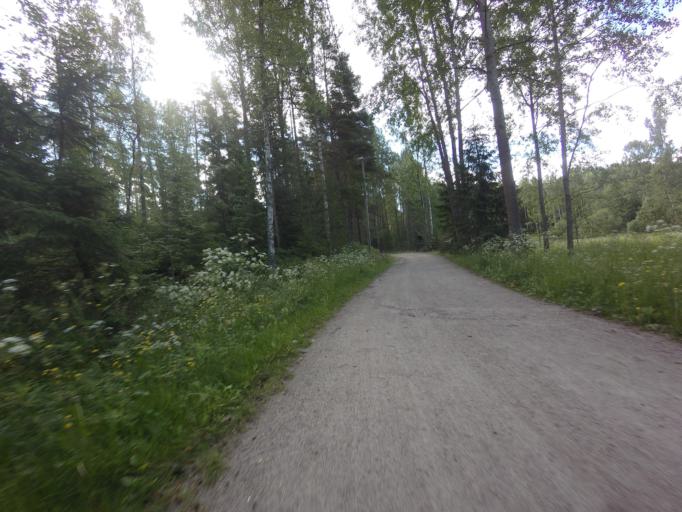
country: FI
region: Uusimaa
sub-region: Helsinki
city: Espoo
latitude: 60.1859
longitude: 24.6366
